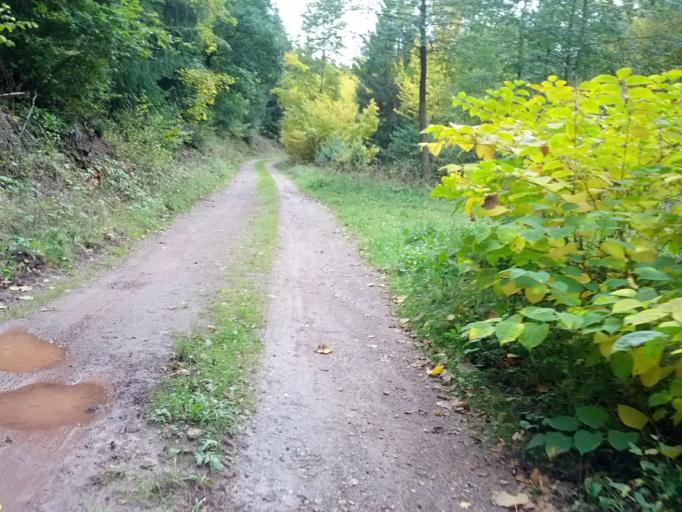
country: DE
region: Thuringia
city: Eisenach
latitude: 50.9750
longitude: 10.2758
